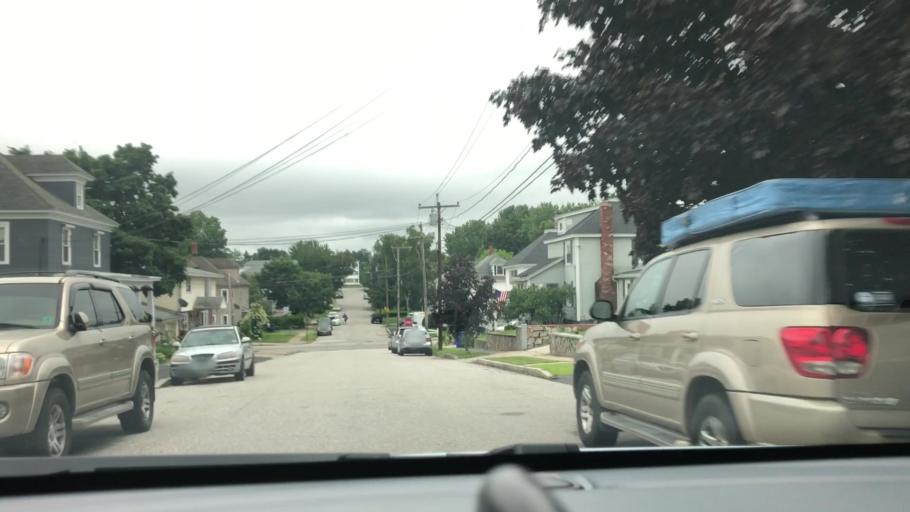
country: US
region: New Hampshire
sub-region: Hillsborough County
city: Pinardville
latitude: 42.9958
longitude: -71.4886
